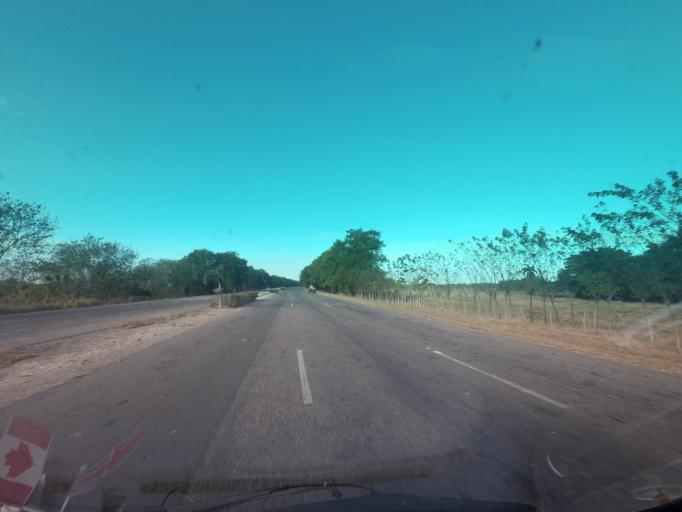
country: CU
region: Cienfuegos
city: Rodas
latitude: 22.4414
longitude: -80.5116
